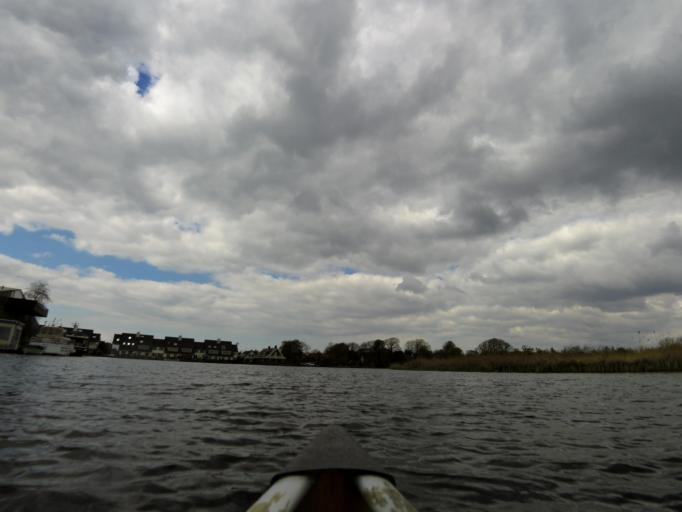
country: NL
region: South Holland
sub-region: Gemeente Leiden
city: Leiden
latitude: 52.1915
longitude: 4.5024
